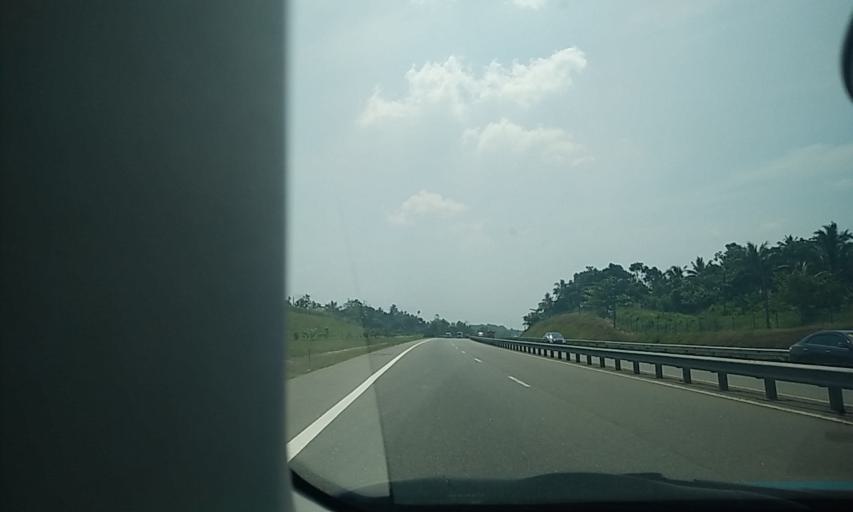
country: LK
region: Western
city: Horana South
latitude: 6.7472
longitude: 79.9973
